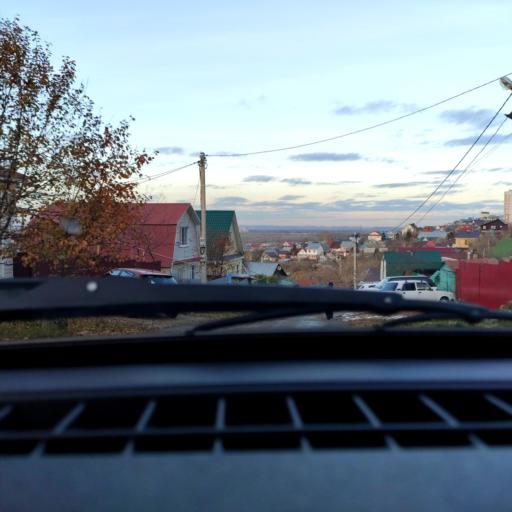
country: RU
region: Bashkortostan
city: Ufa
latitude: 54.7342
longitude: 55.9245
